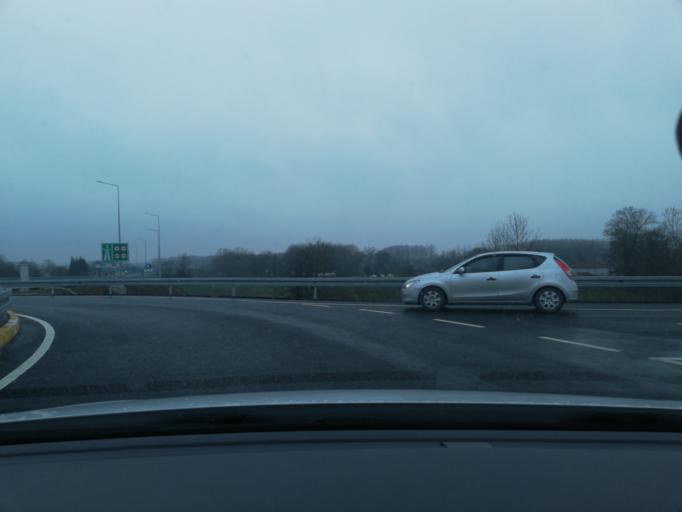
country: TR
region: Duzce
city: Duzce
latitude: 40.8057
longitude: 31.1683
